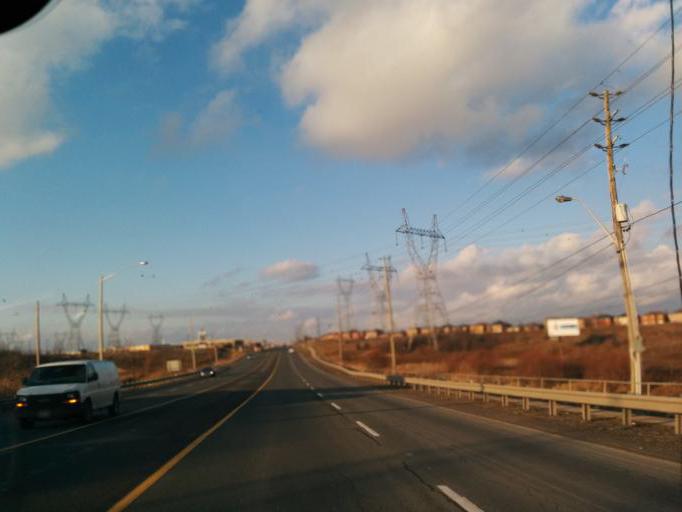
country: CA
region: Ontario
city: Etobicoke
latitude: 43.7787
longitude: -79.6228
